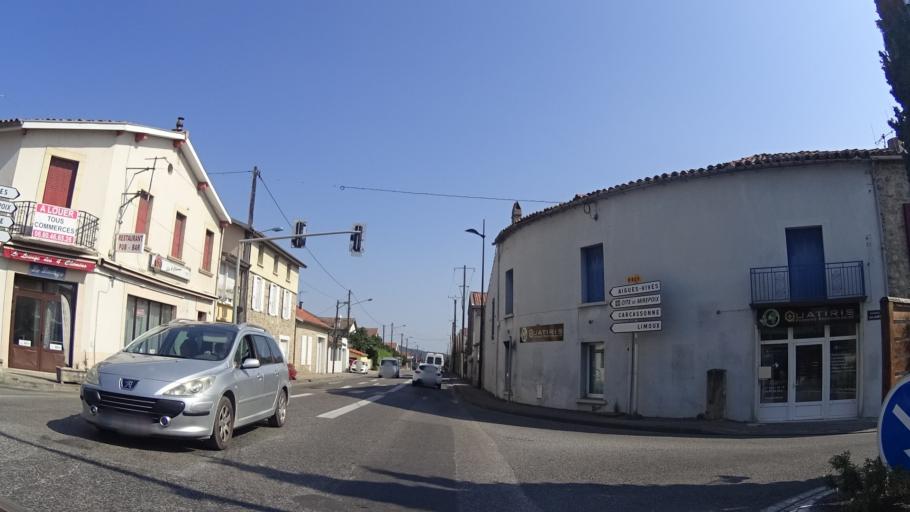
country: FR
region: Midi-Pyrenees
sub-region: Departement de l'Ariege
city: Lavelanet
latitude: 42.9712
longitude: 1.8667
